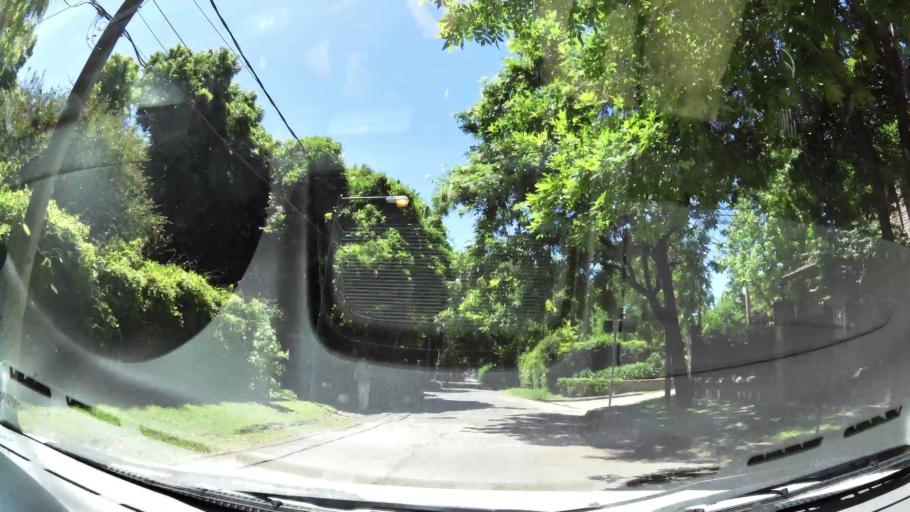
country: AR
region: Buenos Aires
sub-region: Partido de Tigre
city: Tigre
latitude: -34.4916
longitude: -58.5732
